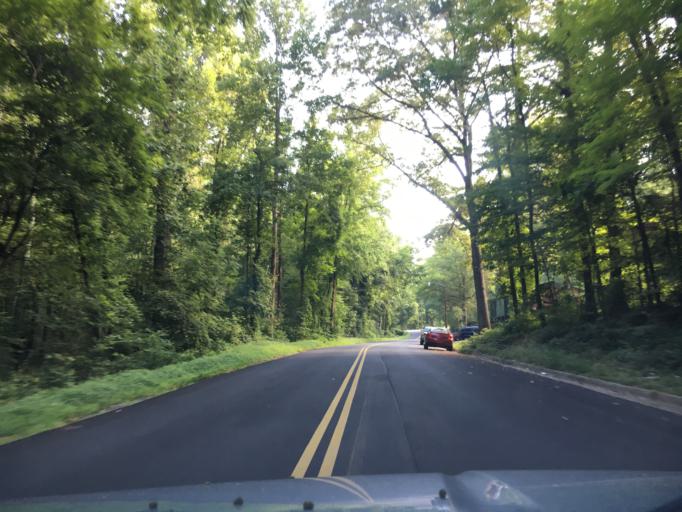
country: US
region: Virginia
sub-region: Halifax County
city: South Boston
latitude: 36.7083
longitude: -78.9135
